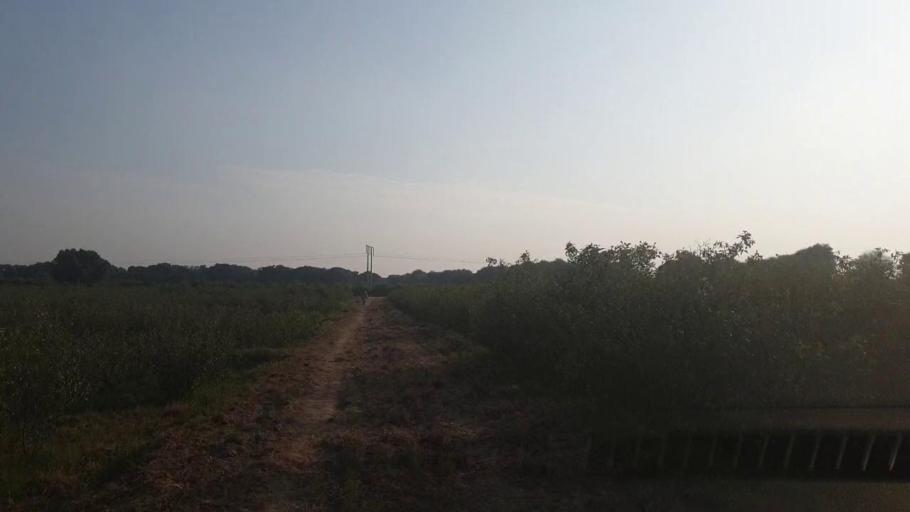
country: PK
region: Sindh
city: Tando Jam
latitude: 25.4263
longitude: 68.4621
